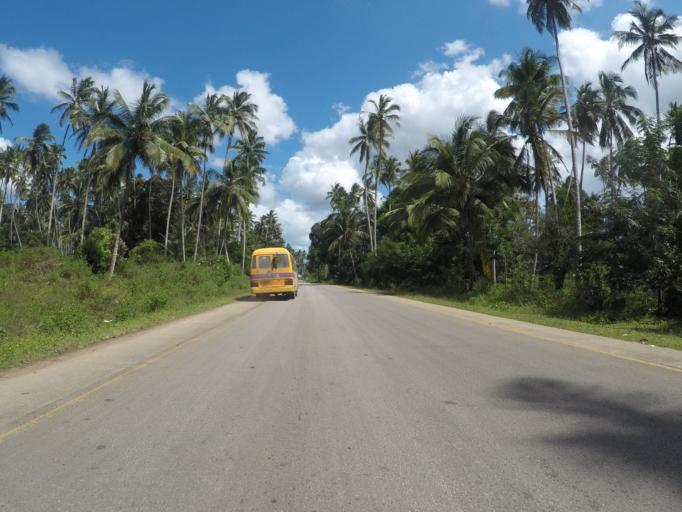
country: TZ
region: Zanzibar Central/South
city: Koani
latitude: -6.1494
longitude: 39.3294
